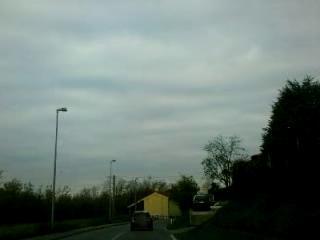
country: IT
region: Lombardy
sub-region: Provincia di Brescia
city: Capriano del Colle
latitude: 45.4689
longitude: 10.1228
